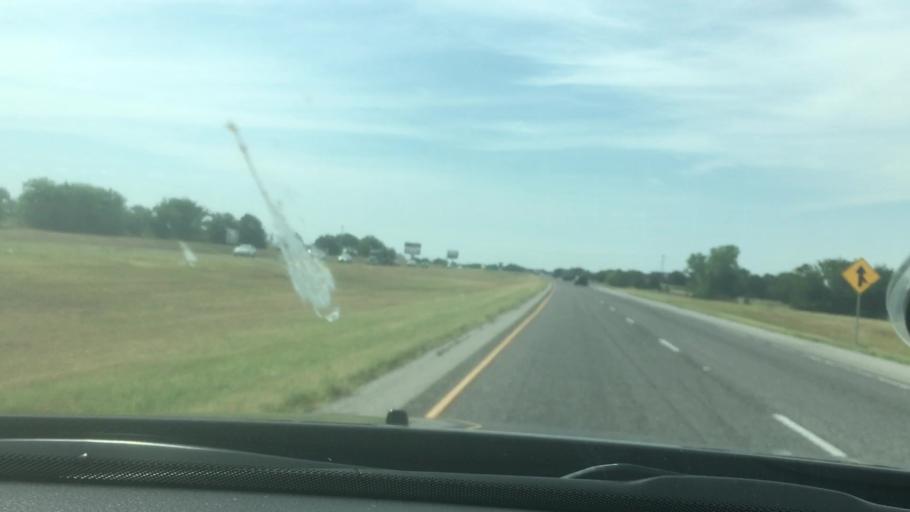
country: US
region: Oklahoma
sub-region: Garvin County
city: Wynnewood
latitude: 34.5698
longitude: -97.1984
